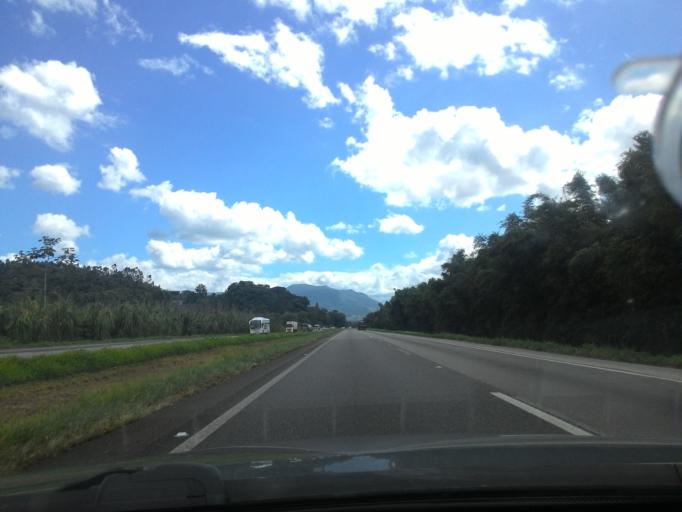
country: BR
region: Sao Paulo
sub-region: Jacupiranga
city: Jacupiranga
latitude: -24.7192
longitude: -48.0397
